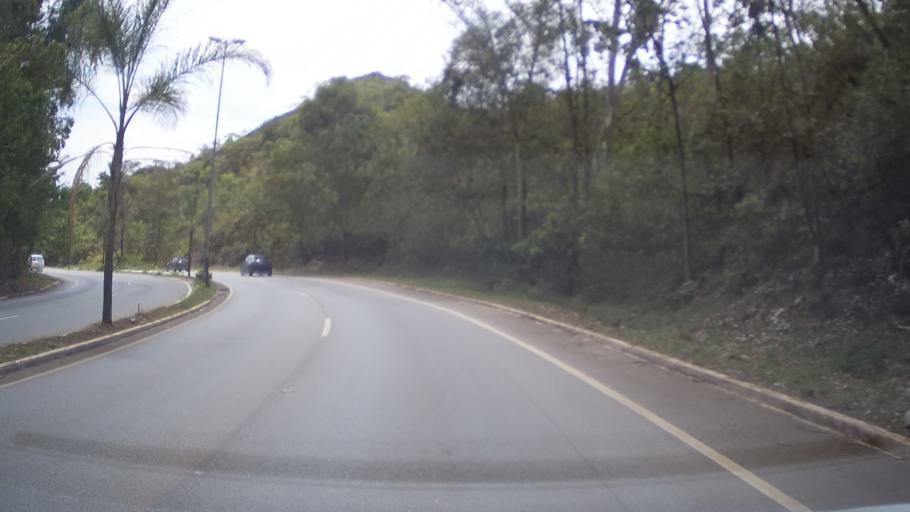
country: BR
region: Minas Gerais
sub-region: Nova Lima
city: Nova Lima
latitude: -20.0017
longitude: -43.9019
